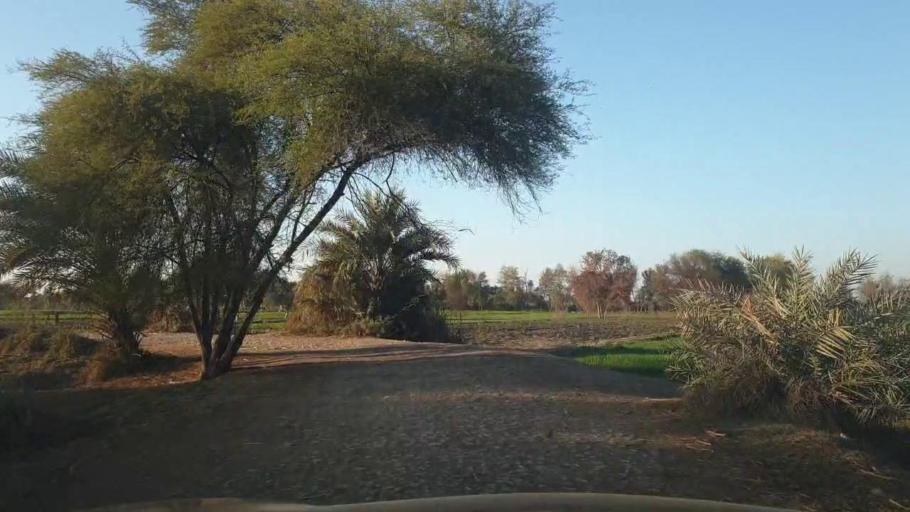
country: PK
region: Sindh
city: Mirpur Mathelo
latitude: 28.0055
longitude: 69.4648
